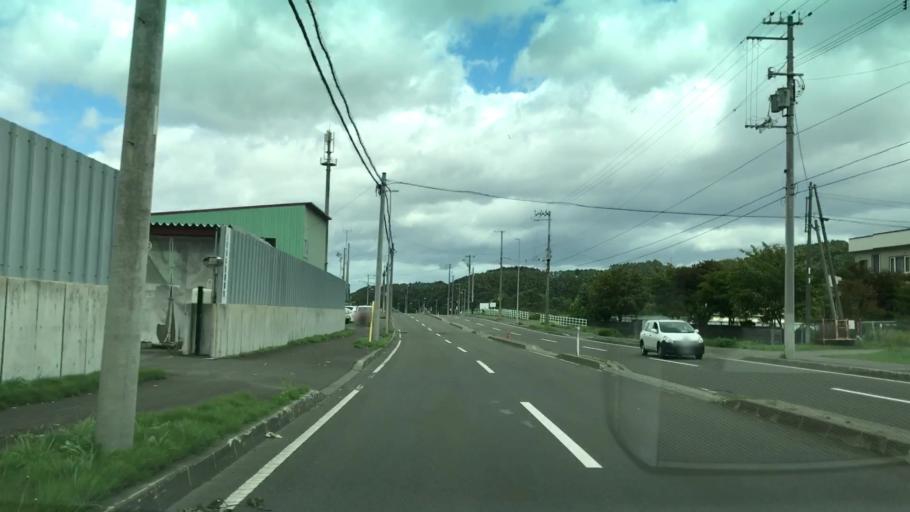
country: JP
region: Hokkaido
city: Kitahiroshima
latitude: 42.9724
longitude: 141.4510
